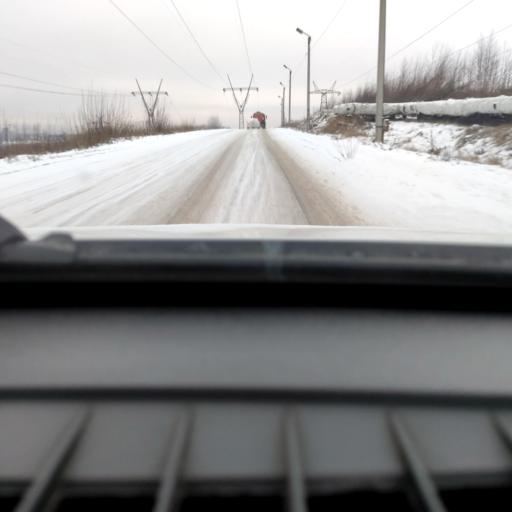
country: RU
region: Perm
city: Perm
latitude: 58.1070
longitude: 56.3691
